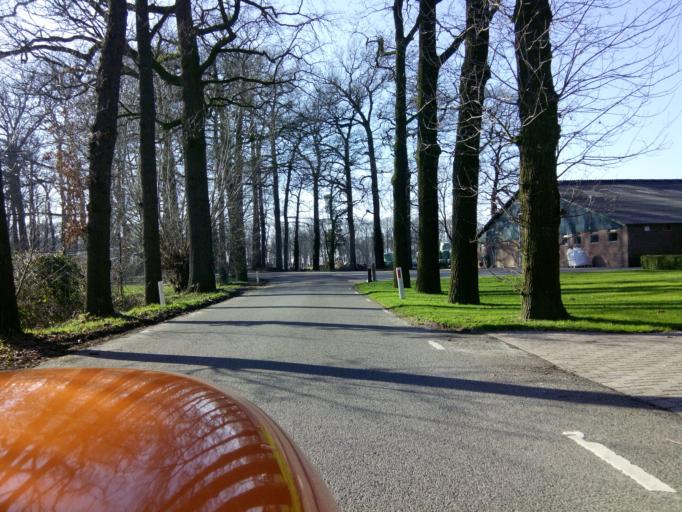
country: NL
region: Utrecht
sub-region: Gemeente Leusden
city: Leusden
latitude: 52.1035
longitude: 5.4675
